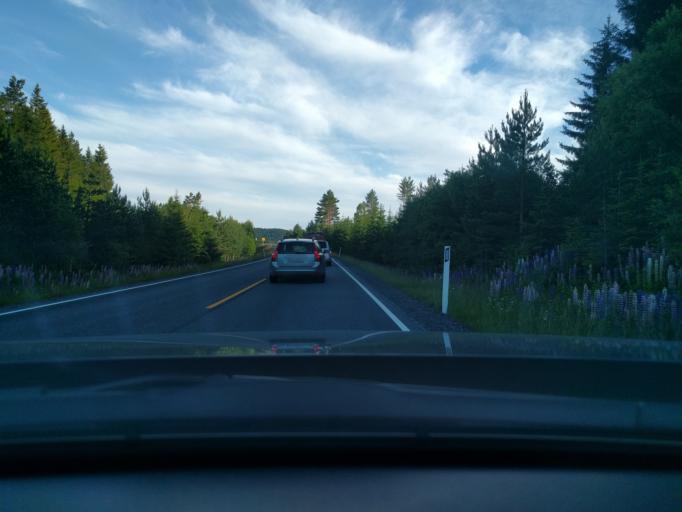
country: NO
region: Buskerud
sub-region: Kongsberg
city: Hvittingfoss
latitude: 59.4624
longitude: 10.0188
